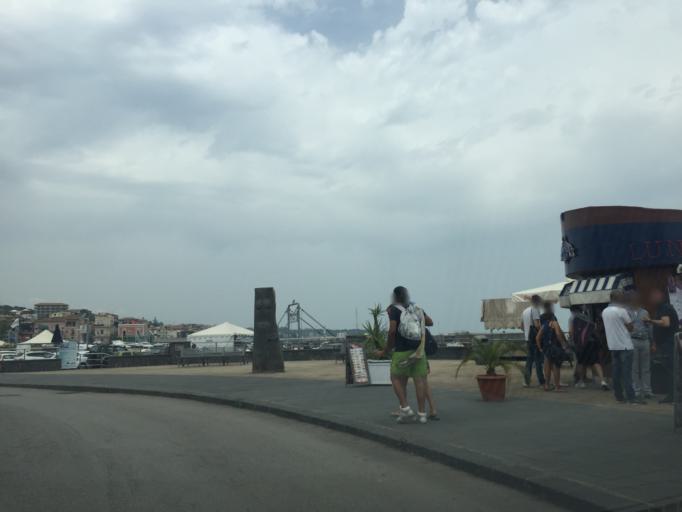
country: IT
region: Sicily
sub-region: Catania
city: Acitrezza
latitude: 37.5609
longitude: 15.1617
